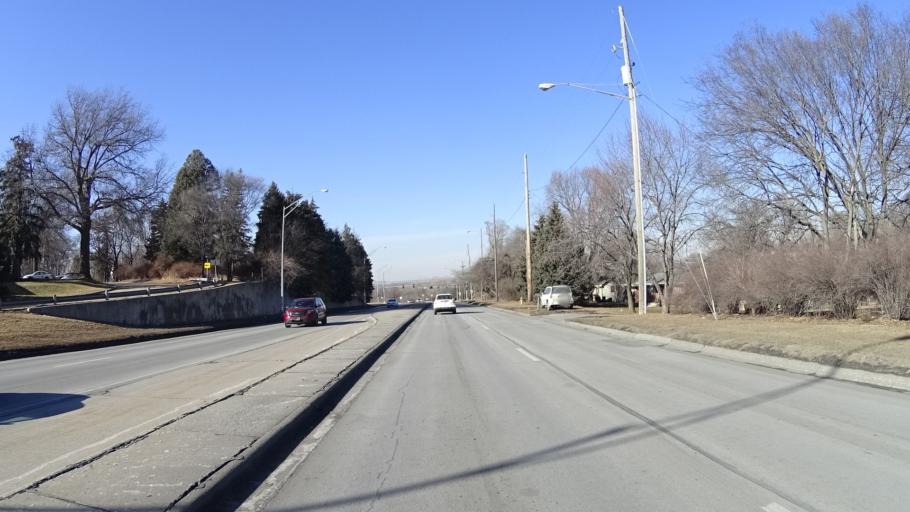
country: US
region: Nebraska
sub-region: Douglas County
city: Ralston
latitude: 41.3051
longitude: -96.0362
